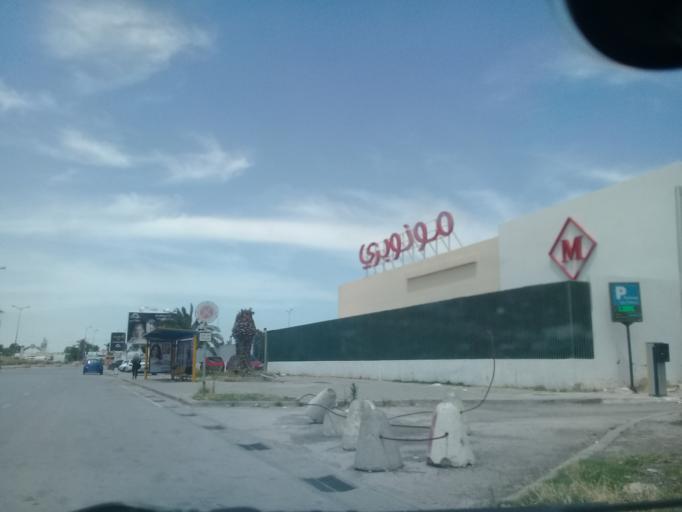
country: TN
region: Ariana
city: Ariana
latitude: 36.8382
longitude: 10.2376
